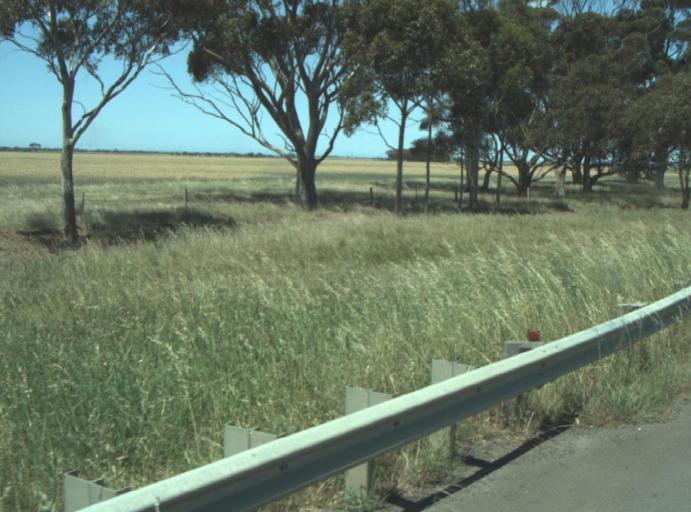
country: AU
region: Victoria
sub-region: Greater Geelong
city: Lara
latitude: -37.9437
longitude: 144.3565
